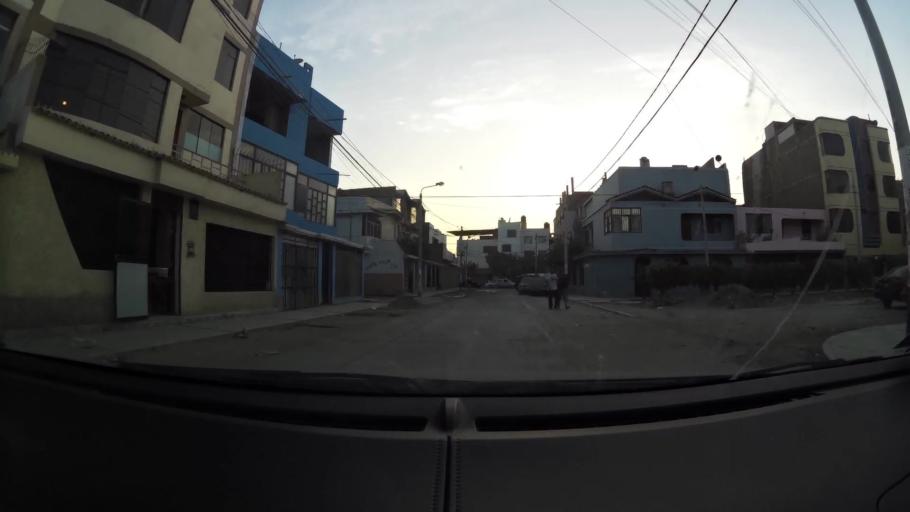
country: PE
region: Lambayeque
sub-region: Provincia de Chiclayo
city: Santa Rosa
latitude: -6.7662
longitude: -79.8319
